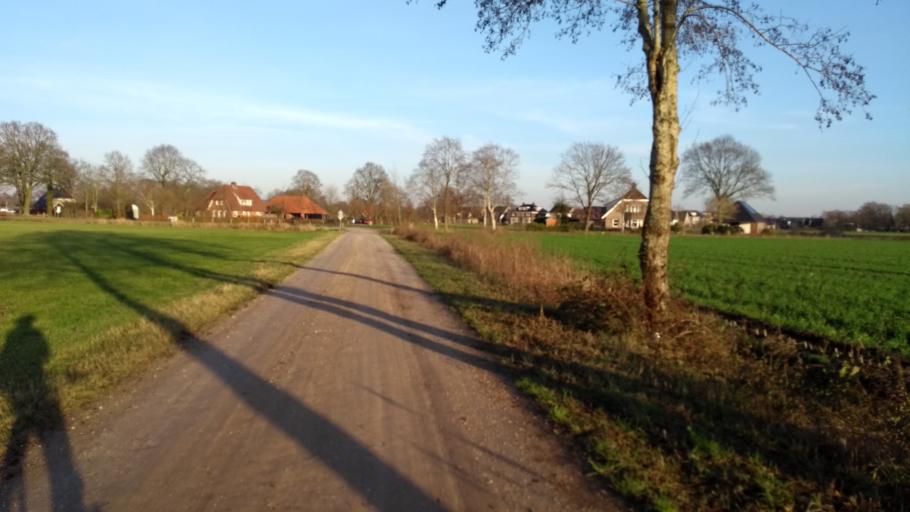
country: NL
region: Overijssel
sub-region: Gemeente Almelo
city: Almelo
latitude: 52.3834
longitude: 6.7053
